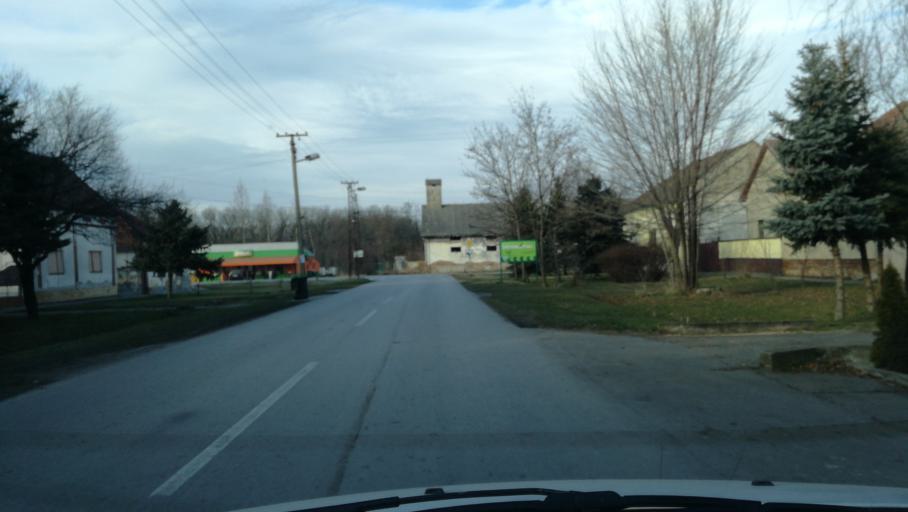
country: RS
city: Banatsko Veliko Selo
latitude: 45.8191
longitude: 20.6073
